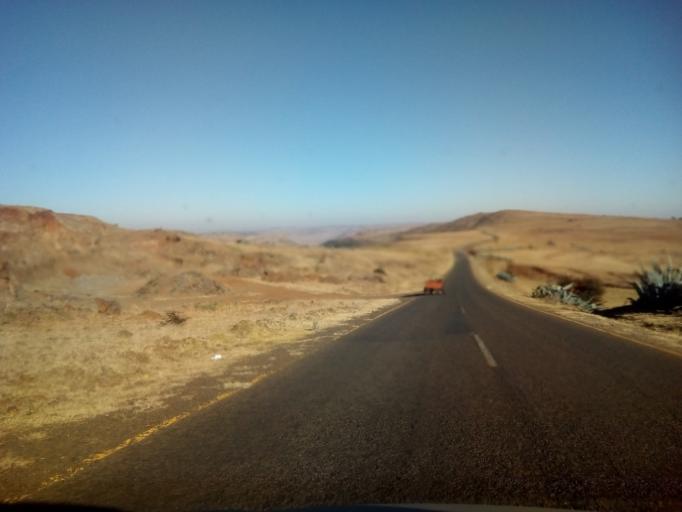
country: LS
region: Berea
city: Teyateyaneng
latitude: -29.2535
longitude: 27.7850
